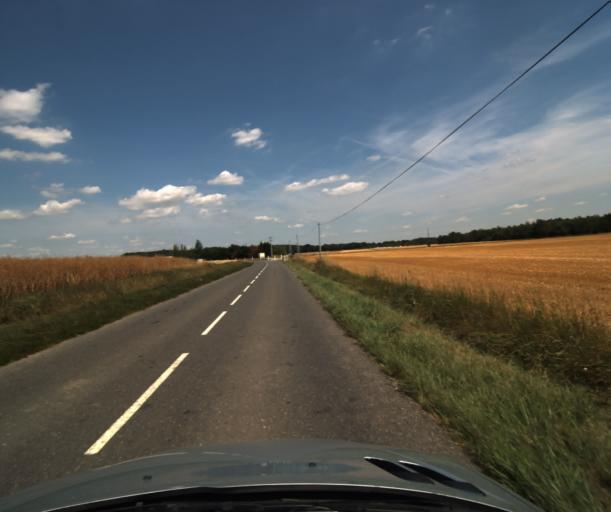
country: FR
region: Midi-Pyrenees
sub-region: Departement de la Haute-Garonne
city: Labastidette
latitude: 43.4835
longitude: 1.2168
